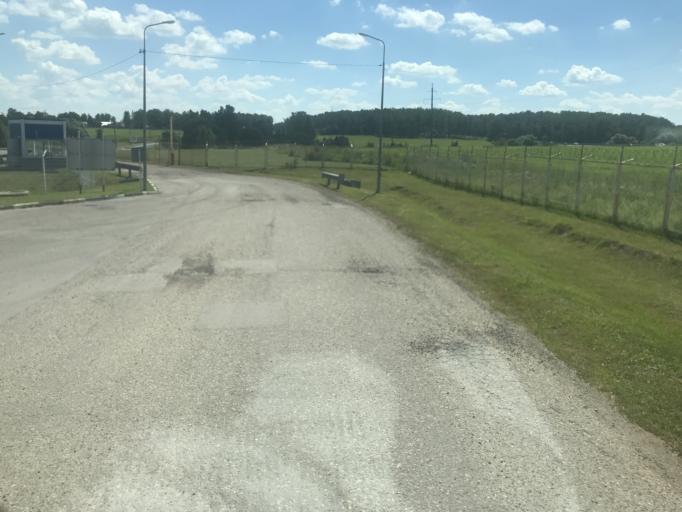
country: RU
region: Moskovskaya
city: Lyubuchany
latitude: 55.2520
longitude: 37.5336
